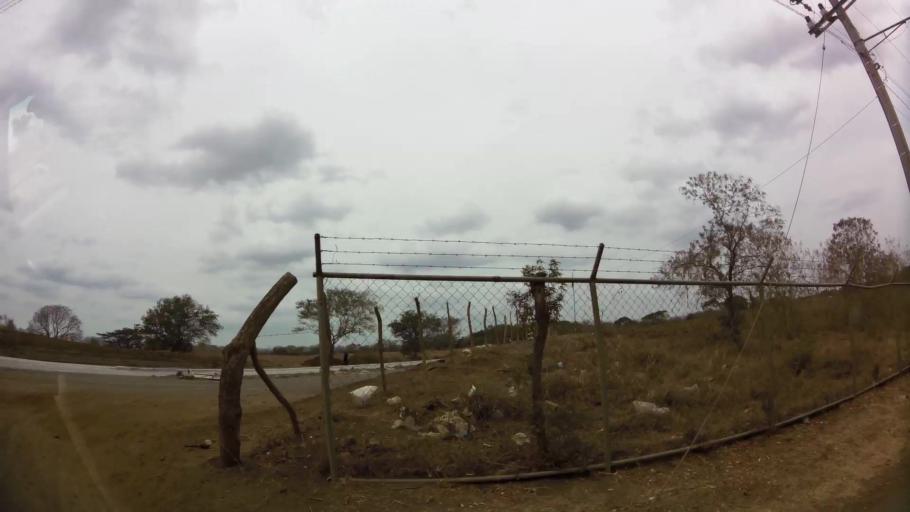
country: NI
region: Masaya
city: Ticuantepe
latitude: 12.0913
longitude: -86.1823
